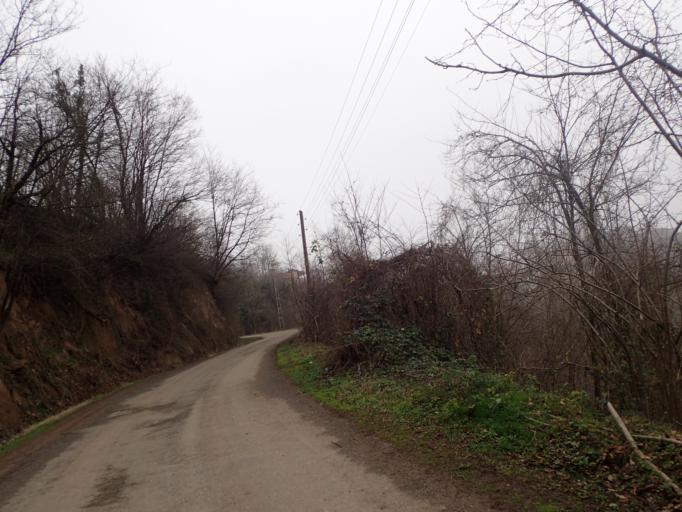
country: TR
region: Ordu
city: Camas
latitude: 40.9218
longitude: 37.5525
